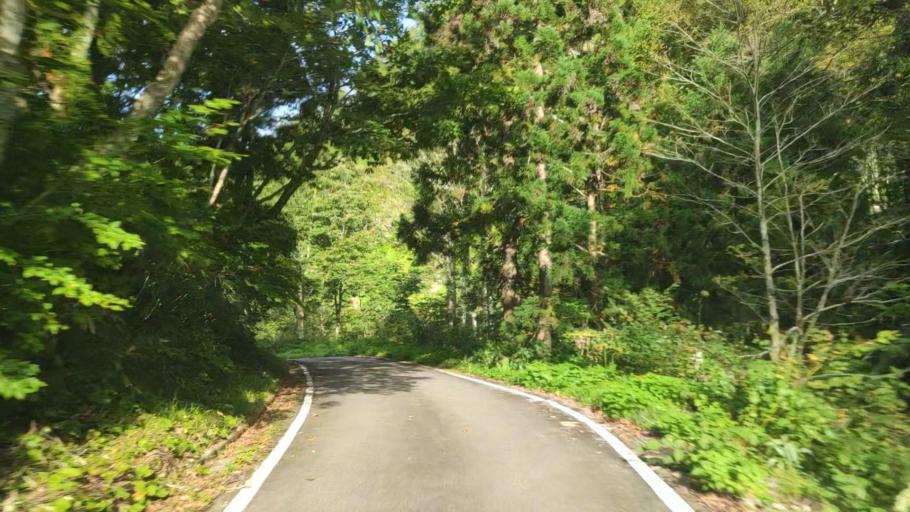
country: JP
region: Toyama
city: Yatsuomachi-higashikumisaka
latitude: 36.3648
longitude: 137.0730
